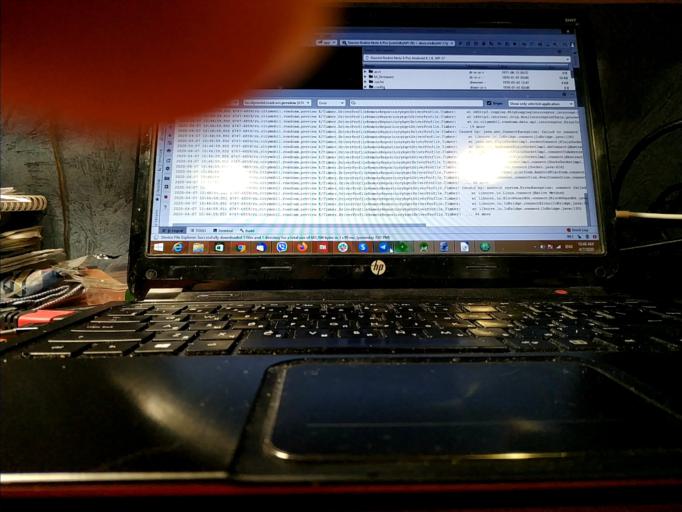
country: RU
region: Vologda
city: Suda
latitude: 58.9220
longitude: 37.5432
